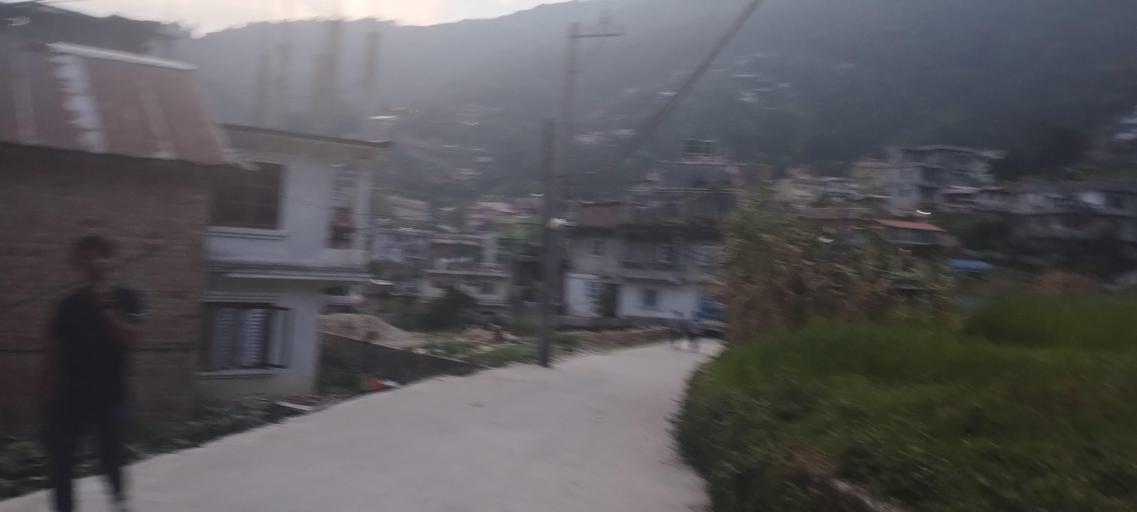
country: NP
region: Central Region
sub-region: Bagmati Zone
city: Kathmandu
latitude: 27.7848
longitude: 85.3599
